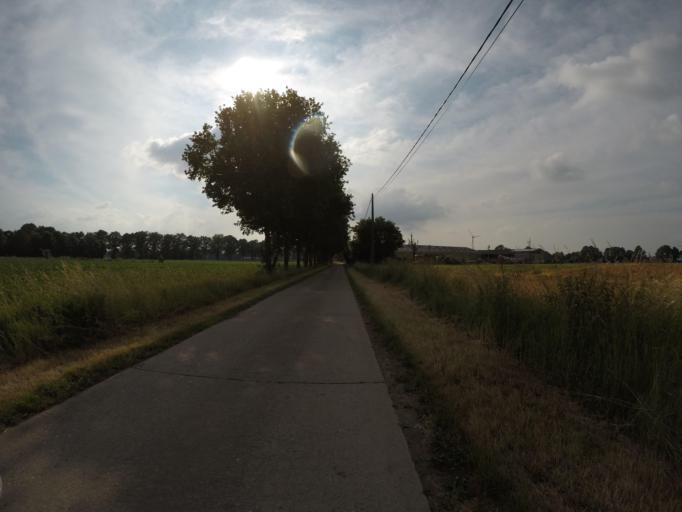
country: BE
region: Flanders
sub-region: Provincie Antwerpen
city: Brecht
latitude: 51.3727
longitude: 4.6826
